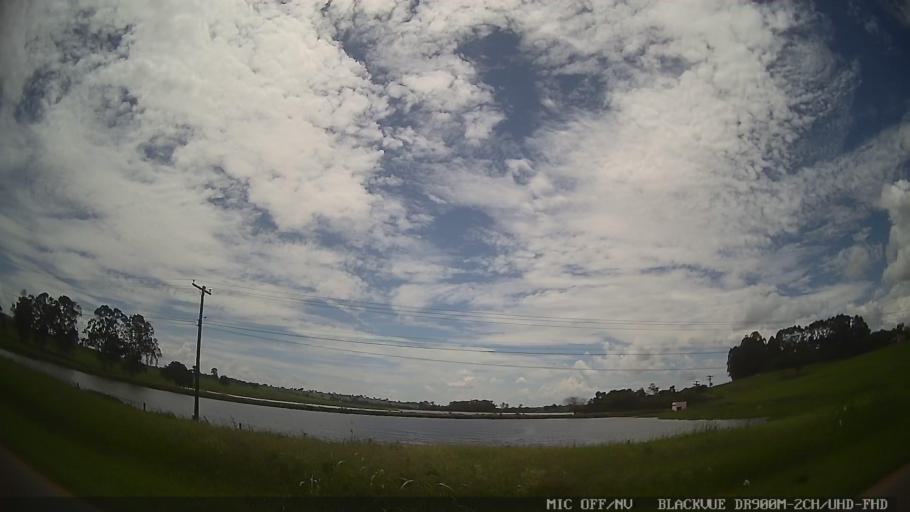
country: BR
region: Sao Paulo
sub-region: Conchas
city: Conchas
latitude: -23.0562
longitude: -47.9618
